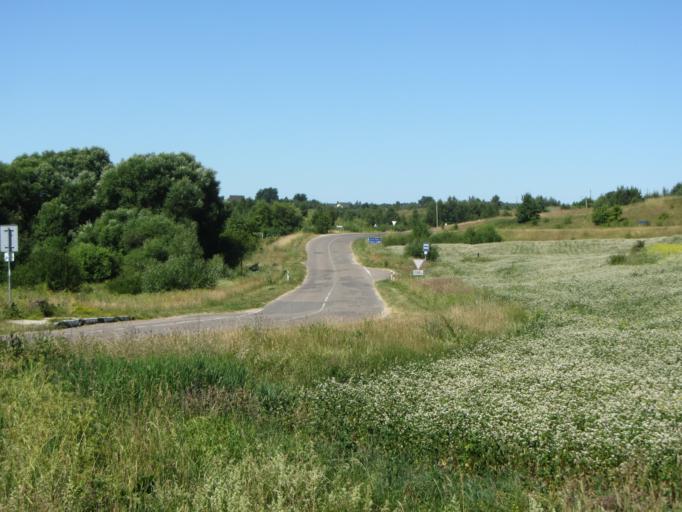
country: LT
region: Vilnius County
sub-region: Trakai
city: Rudiskes
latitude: 54.6388
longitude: 24.8061
